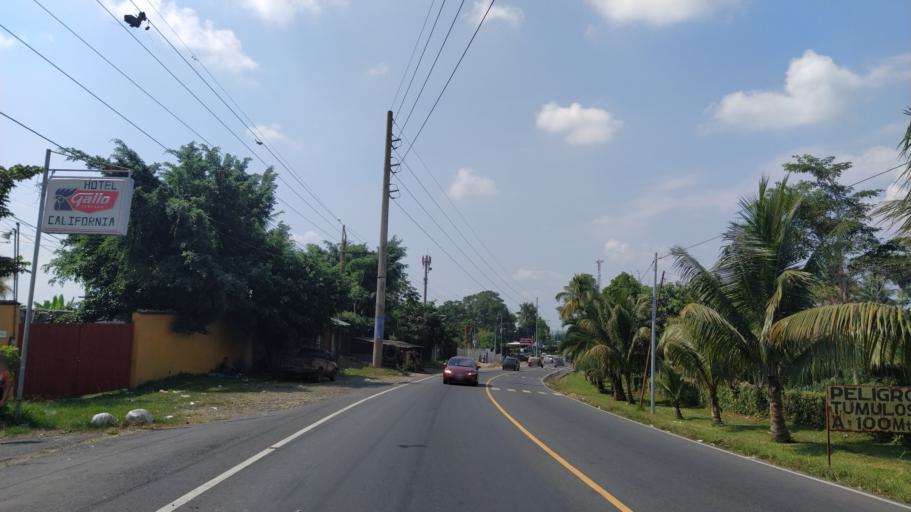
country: GT
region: Retalhuleu
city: San Felipe
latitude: 14.6196
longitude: -91.5924
